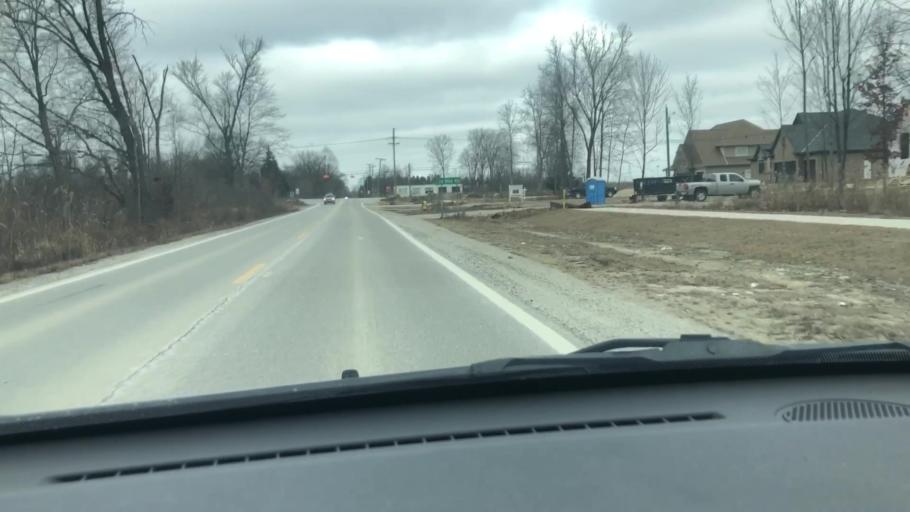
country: US
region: Michigan
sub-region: Macomb County
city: Romeo
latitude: 42.7418
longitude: -83.0174
